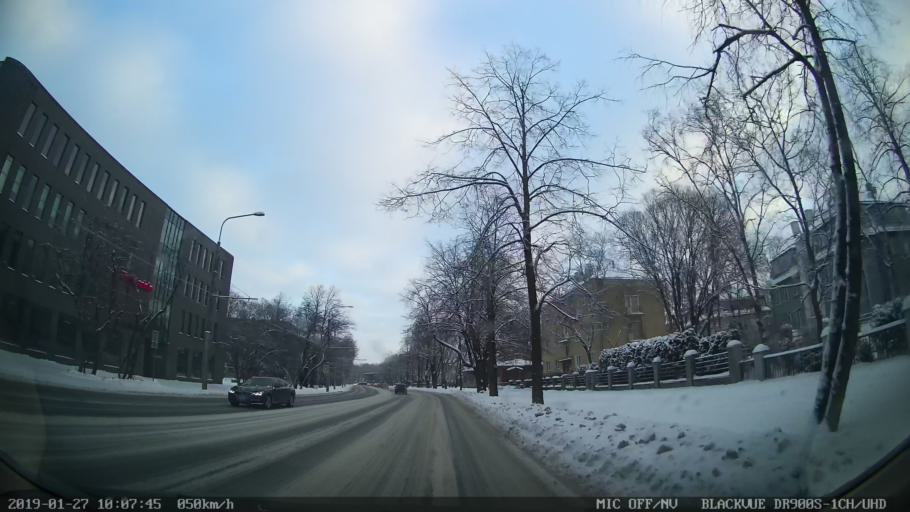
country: EE
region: Harju
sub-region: Tallinna linn
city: Tallinn
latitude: 59.4396
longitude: 24.7810
